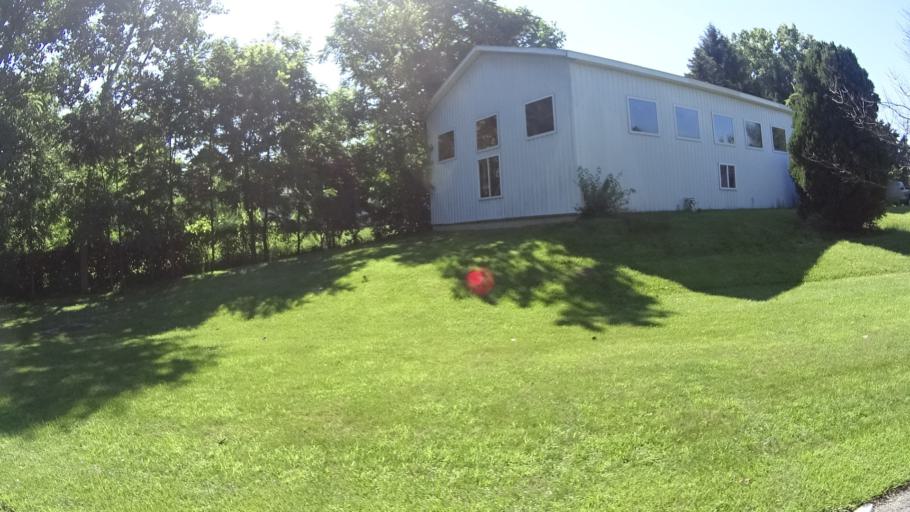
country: US
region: Ohio
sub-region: Erie County
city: Sandusky
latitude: 41.3986
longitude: -82.6526
